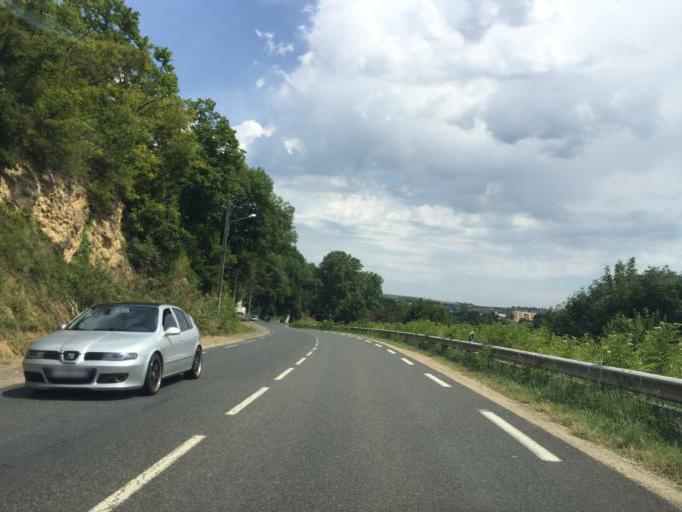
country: FR
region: Rhone-Alpes
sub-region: Departement du Rhone
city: Saint-Germain-Nuelles
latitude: 45.8403
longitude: 4.6016
